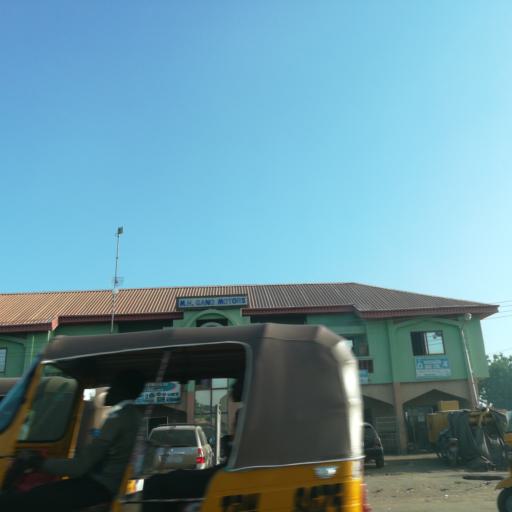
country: NG
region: Kano
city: Kano
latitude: 12.0144
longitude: 8.5029
